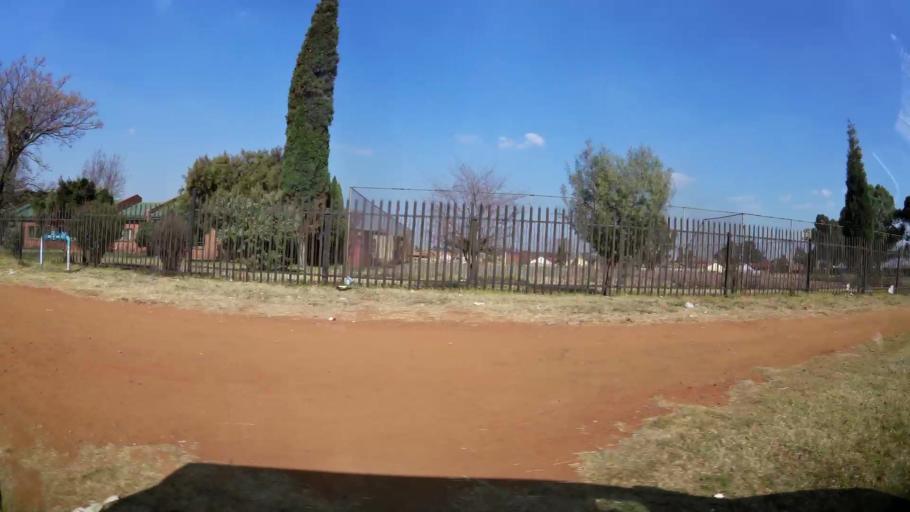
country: ZA
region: Gauteng
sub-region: Ekurhuleni Metropolitan Municipality
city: Brakpan
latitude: -26.1581
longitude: 28.4039
